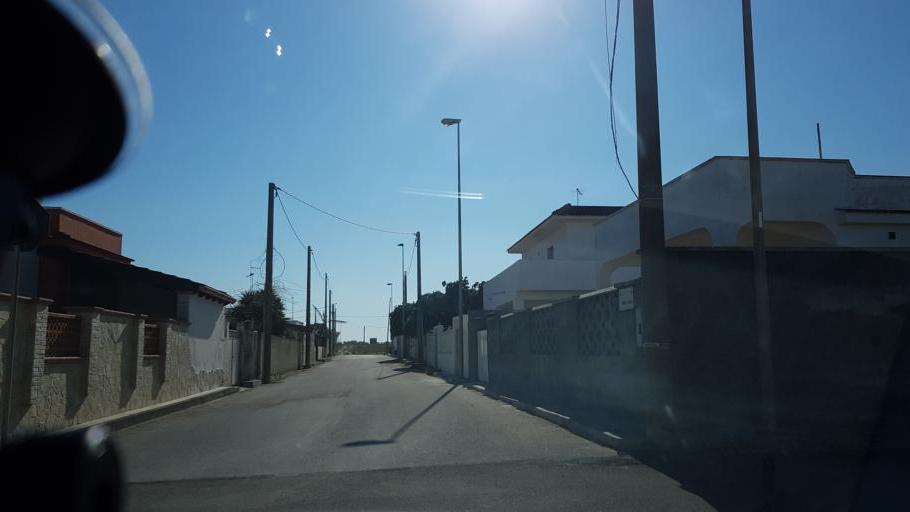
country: IT
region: Apulia
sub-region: Provincia di Brindisi
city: Torchiarolo
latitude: 40.5154
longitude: 18.0960
